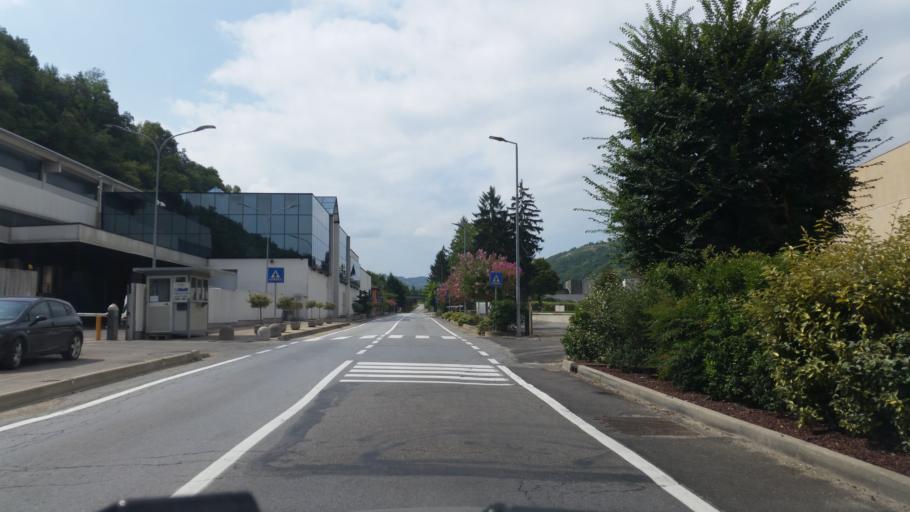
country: IT
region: Piedmont
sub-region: Provincia di Cuneo
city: Cossano Belbo
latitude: 44.6807
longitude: 8.2014
